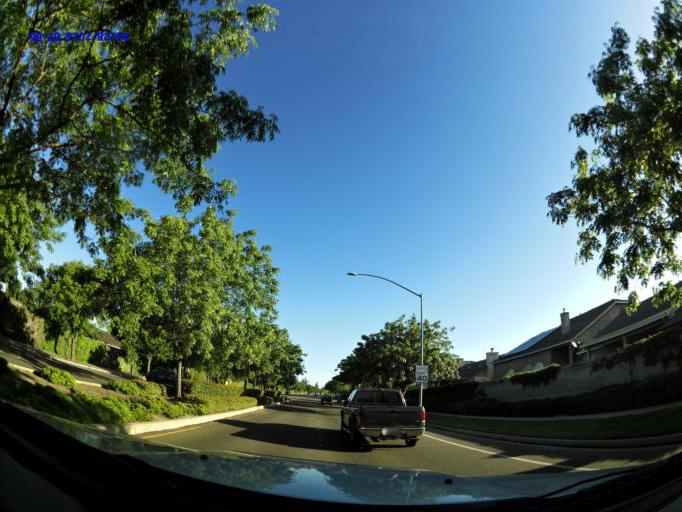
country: US
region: California
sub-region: Stanislaus County
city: Empire
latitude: 37.6682
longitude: -120.9394
